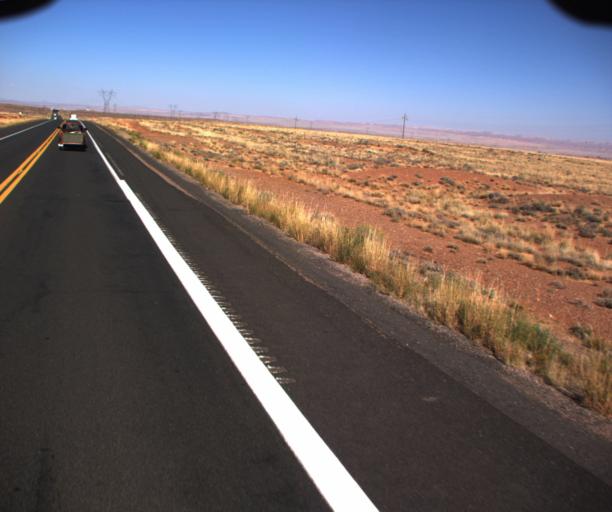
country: US
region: Arizona
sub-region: Coconino County
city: Tuba City
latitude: 35.8118
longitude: -111.4431
